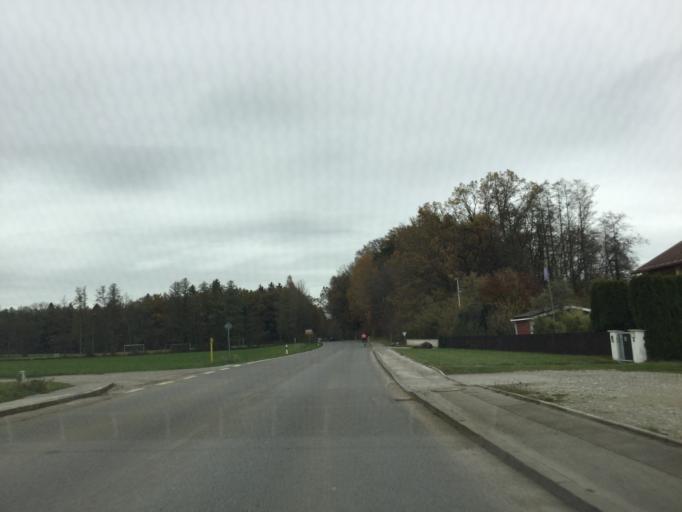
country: DE
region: Bavaria
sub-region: Upper Bavaria
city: Diessen am Ammersee
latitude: 47.9859
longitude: 11.0897
